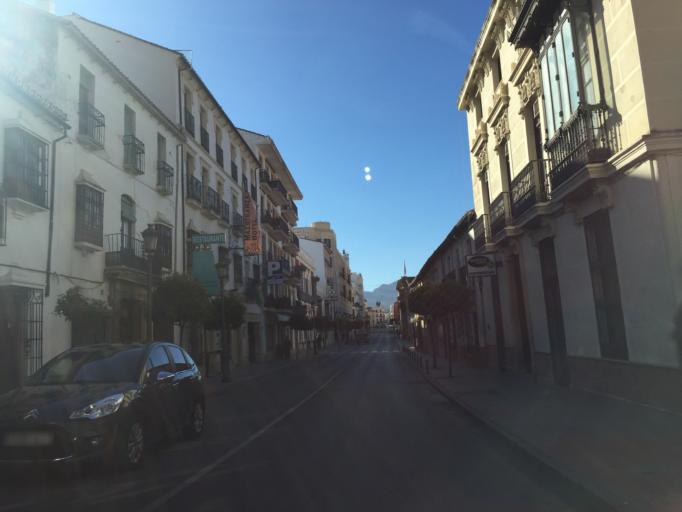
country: ES
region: Andalusia
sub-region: Provincia de Malaga
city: Ronda
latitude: 36.7435
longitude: -5.1670
